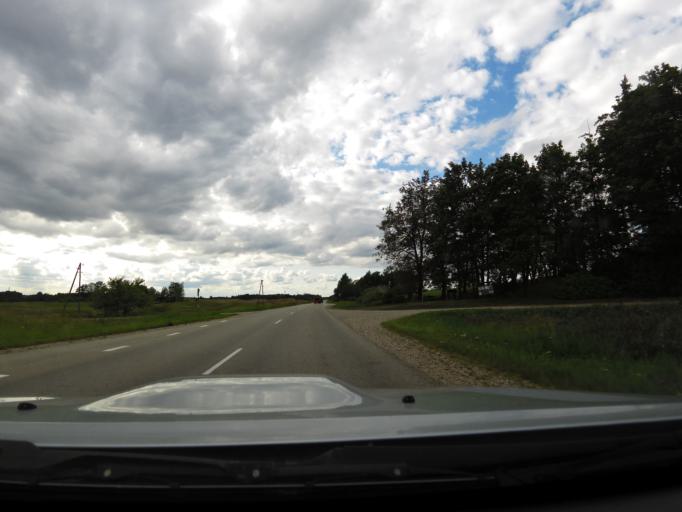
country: LV
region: Akniste
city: Akniste
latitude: 55.9856
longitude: 25.9880
